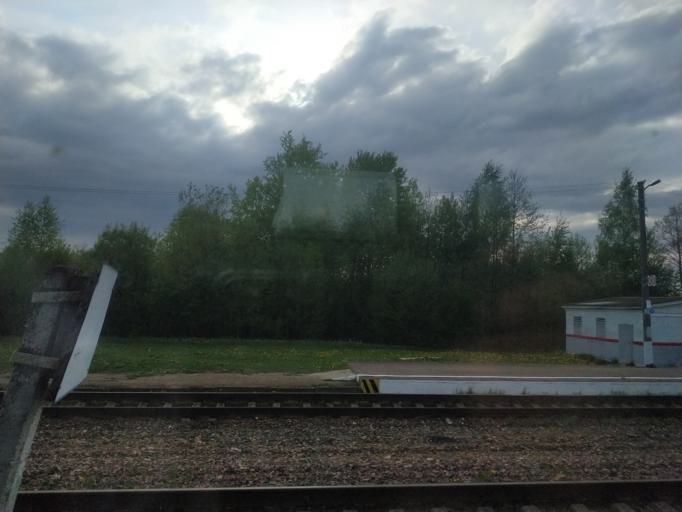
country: RU
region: Smolensk
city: Ugra
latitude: 54.7774
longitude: 34.3423
